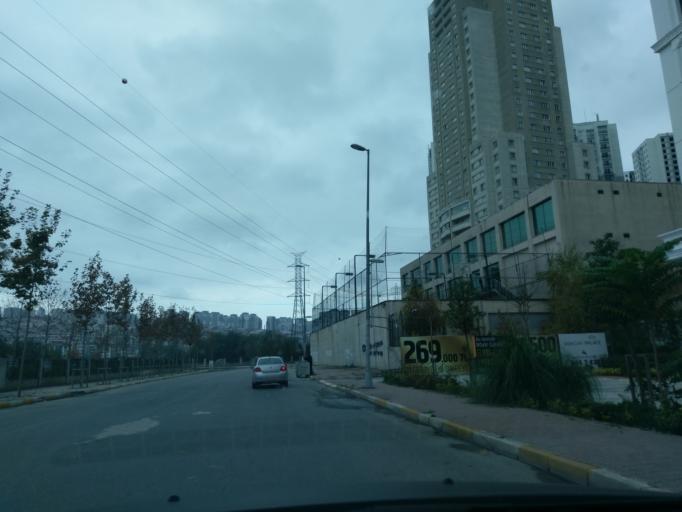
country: TR
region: Istanbul
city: Esenyurt
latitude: 41.0136
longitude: 28.6762
